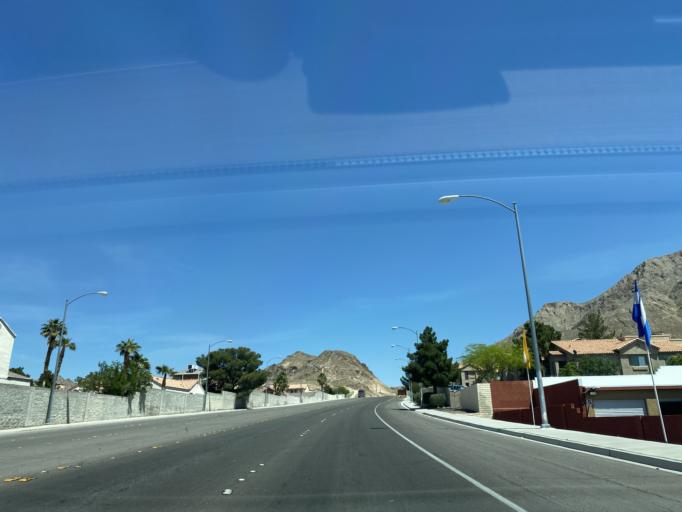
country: US
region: Nevada
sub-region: Clark County
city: Sunrise Manor
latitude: 36.1983
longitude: -115.0161
